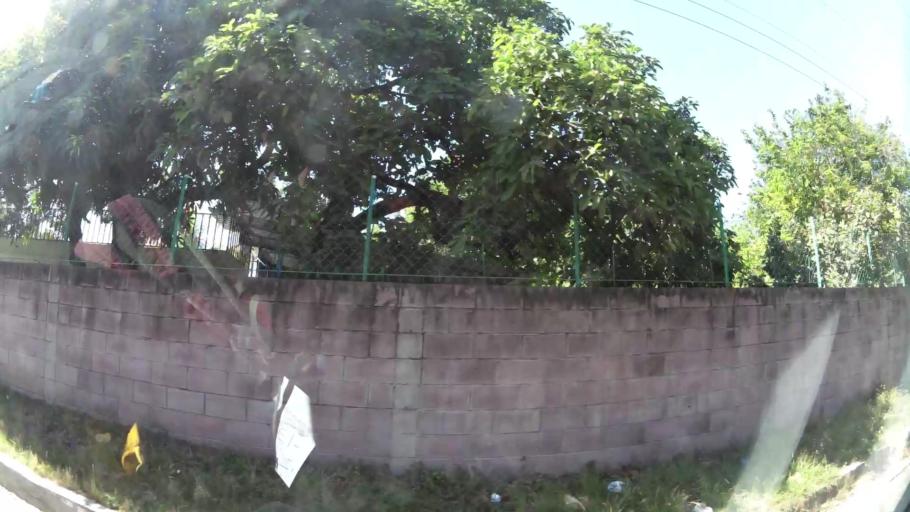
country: SV
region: Sonsonate
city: Armenia
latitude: 13.7339
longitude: -89.3823
